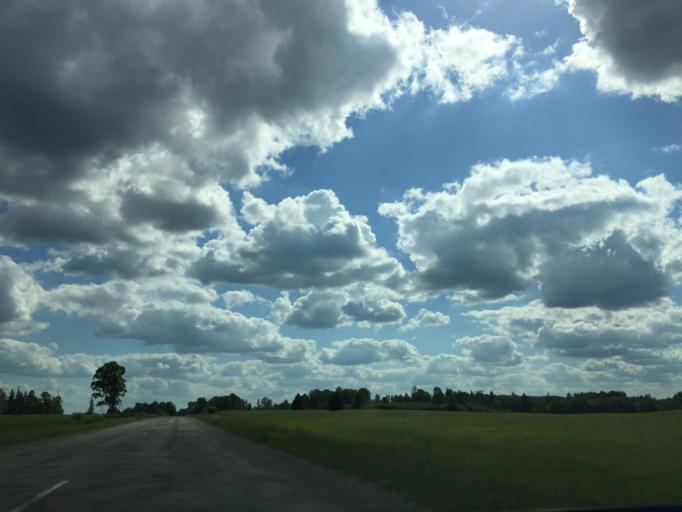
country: LV
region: Jaunpils
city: Jaunpils
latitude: 56.8581
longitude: 23.0526
